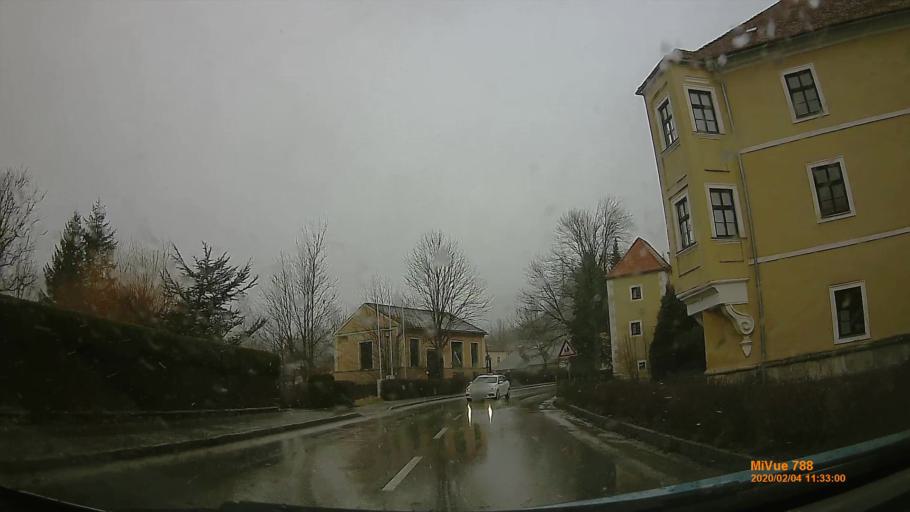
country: AT
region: Styria
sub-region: Politischer Bezirk Bruck-Muerzzuschlag
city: Neuberg an der Muerz
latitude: 47.6624
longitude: 15.5772
